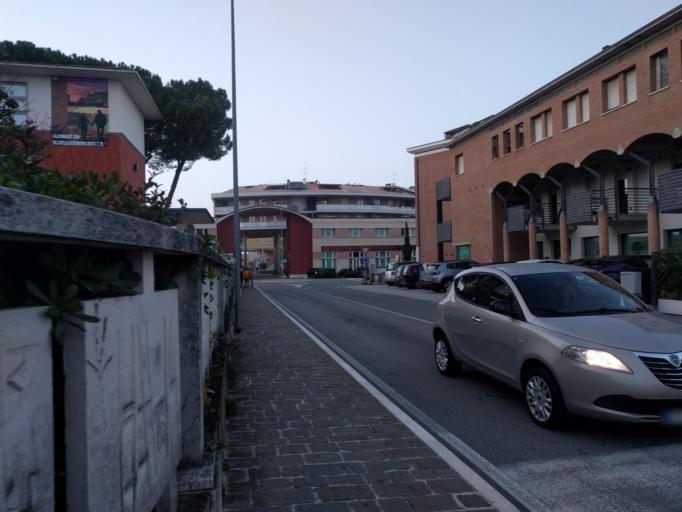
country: IT
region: The Marches
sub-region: Provincia di Ancona
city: Senigallia
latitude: 43.7154
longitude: 13.2135
